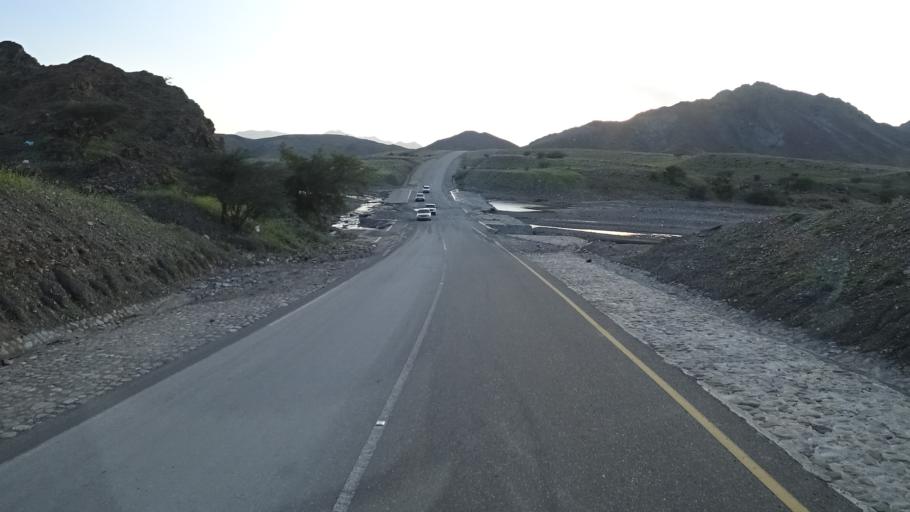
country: OM
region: Al Batinah
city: Al Khaburah
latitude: 23.7989
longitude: 56.9880
